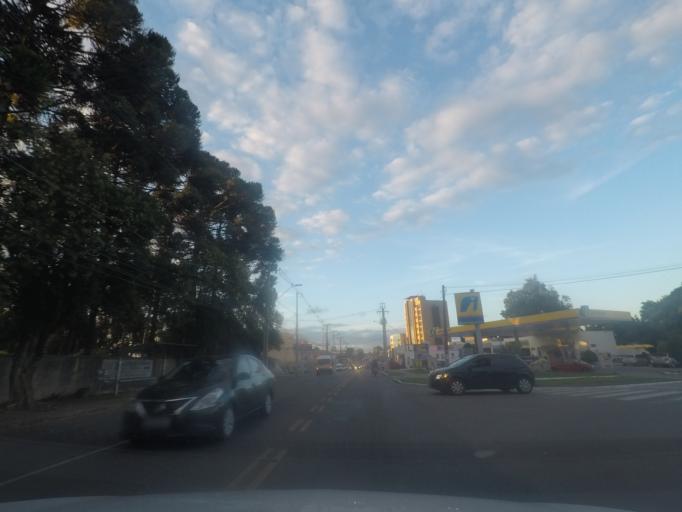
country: BR
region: Parana
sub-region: Pinhais
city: Pinhais
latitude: -25.4424
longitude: -49.1882
